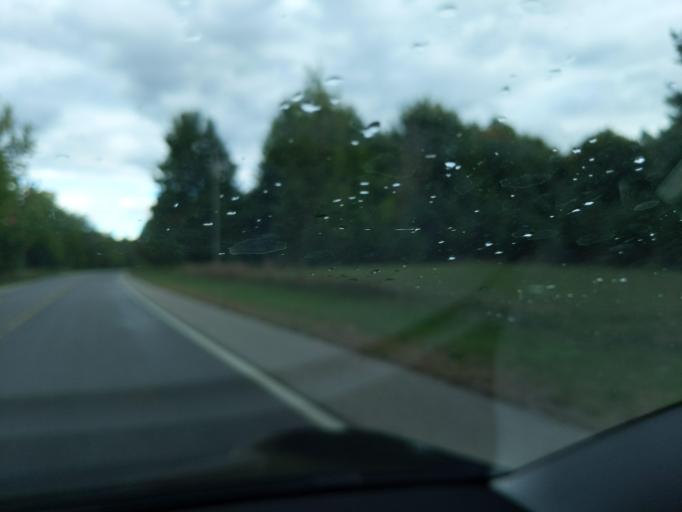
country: US
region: Michigan
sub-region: Kalkaska County
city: Rapid City
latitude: 44.8006
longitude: -85.2735
